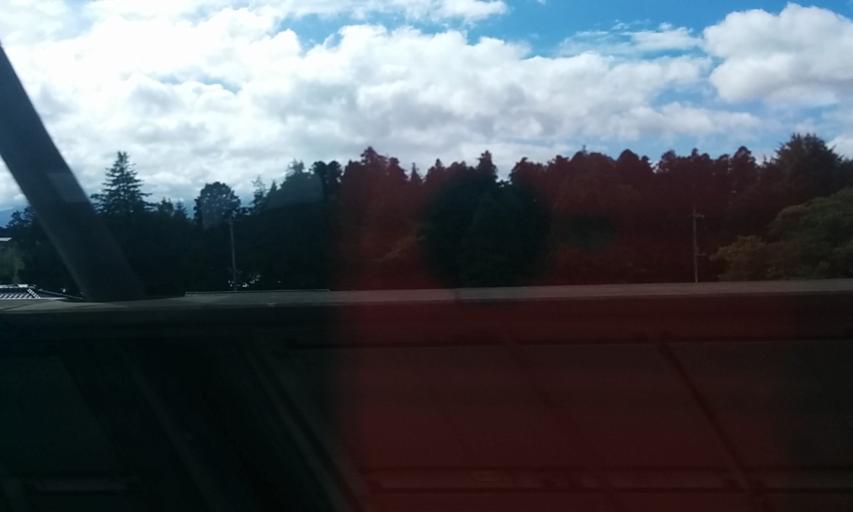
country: JP
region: Tochigi
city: Kuroiso
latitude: 36.9573
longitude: 140.0485
